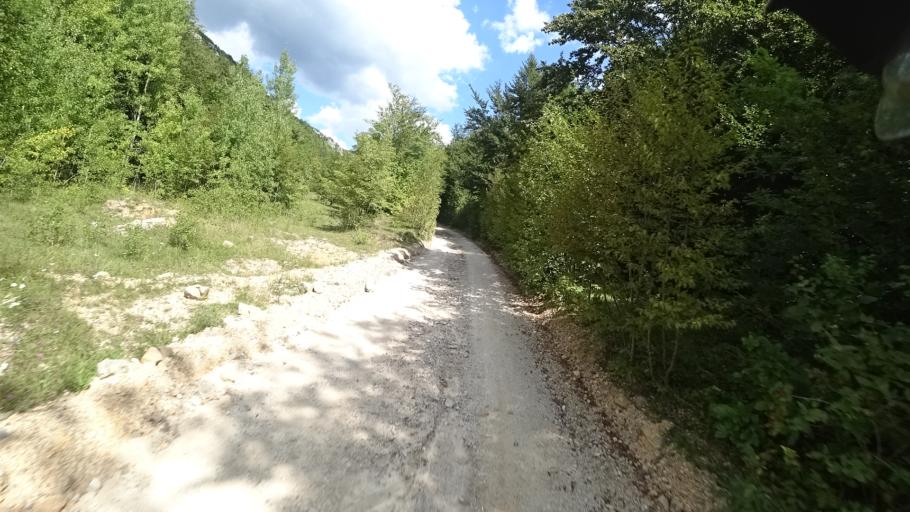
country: BA
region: Federation of Bosnia and Herzegovina
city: Orasac
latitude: 44.5574
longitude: 15.8272
